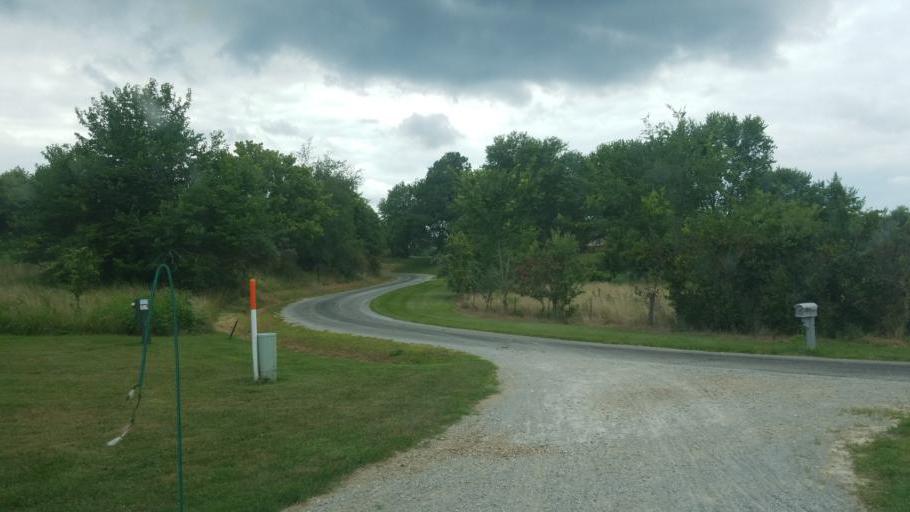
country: US
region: Illinois
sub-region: Jackson County
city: Murphysboro
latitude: 37.7172
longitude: -89.3262
